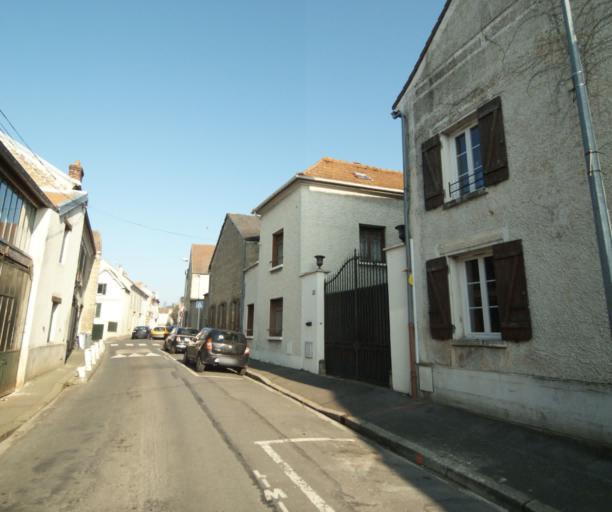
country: FR
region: Ile-de-France
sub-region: Departement du Val-d'Oise
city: Cergy
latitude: 49.0411
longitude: 2.0592
